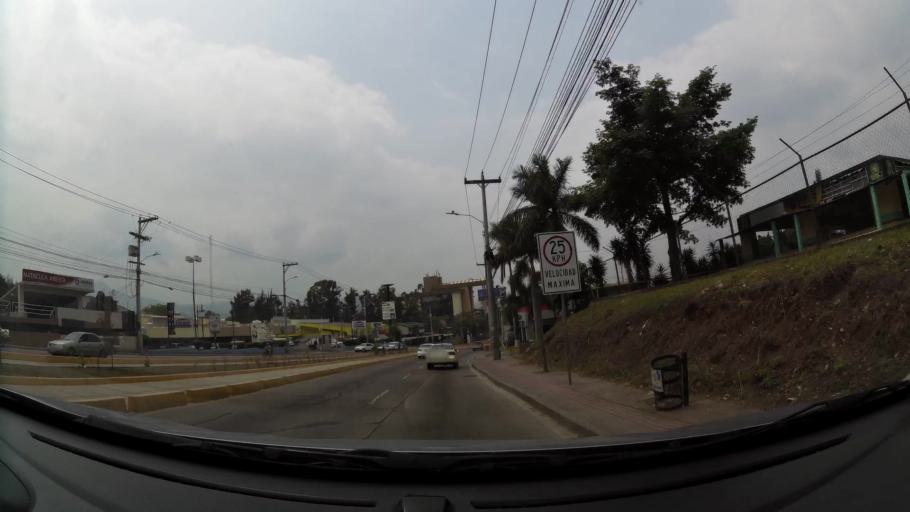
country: HN
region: Francisco Morazan
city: Tegucigalpa
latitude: 14.0832
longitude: -87.1861
